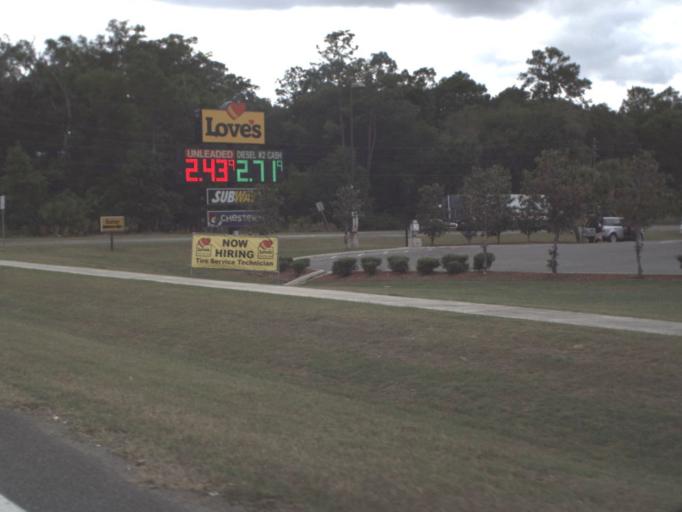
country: US
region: Florida
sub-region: Marion County
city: Ocala
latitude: 29.2671
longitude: -82.1984
